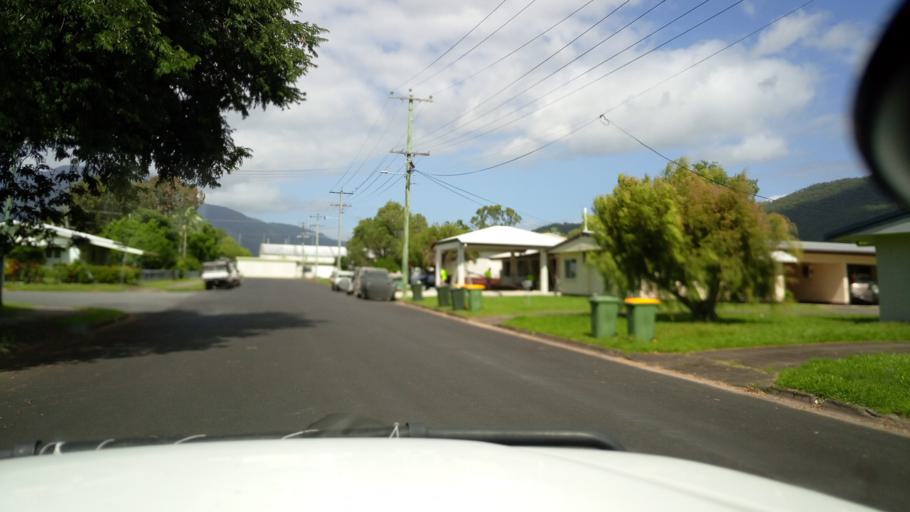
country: AU
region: Queensland
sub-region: Cairns
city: Woree
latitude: -17.0876
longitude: 145.7809
